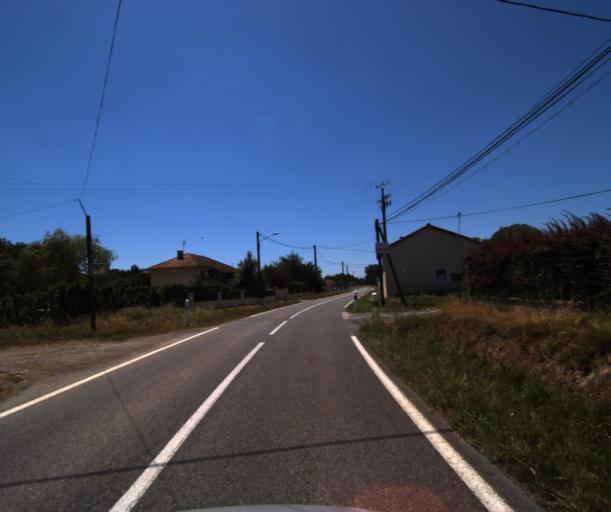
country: FR
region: Midi-Pyrenees
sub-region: Departement de la Haute-Garonne
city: Seysses
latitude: 43.4671
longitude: 1.3015
